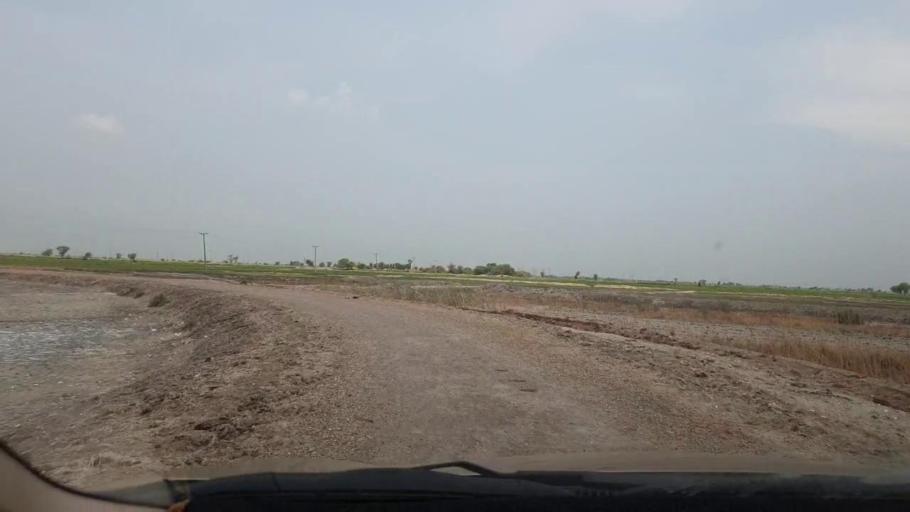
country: PK
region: Sindh
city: Larkana
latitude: 27.5186
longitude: 68.1249
